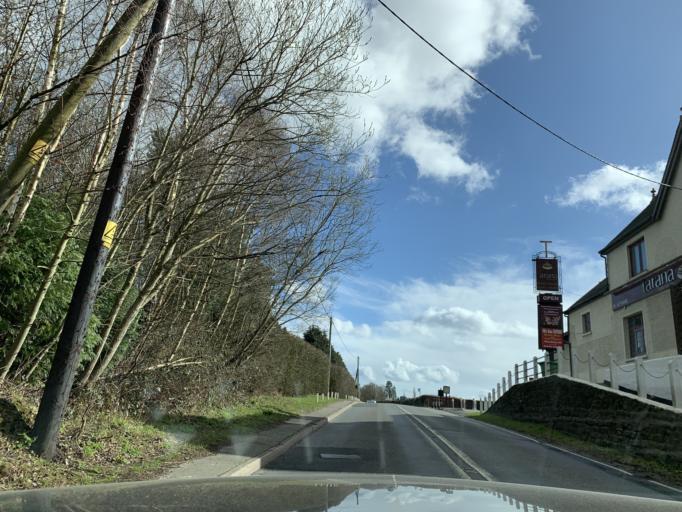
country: GB
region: England
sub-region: West Sussex
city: Crawley Down
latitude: 51.0981
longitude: -0.0838
